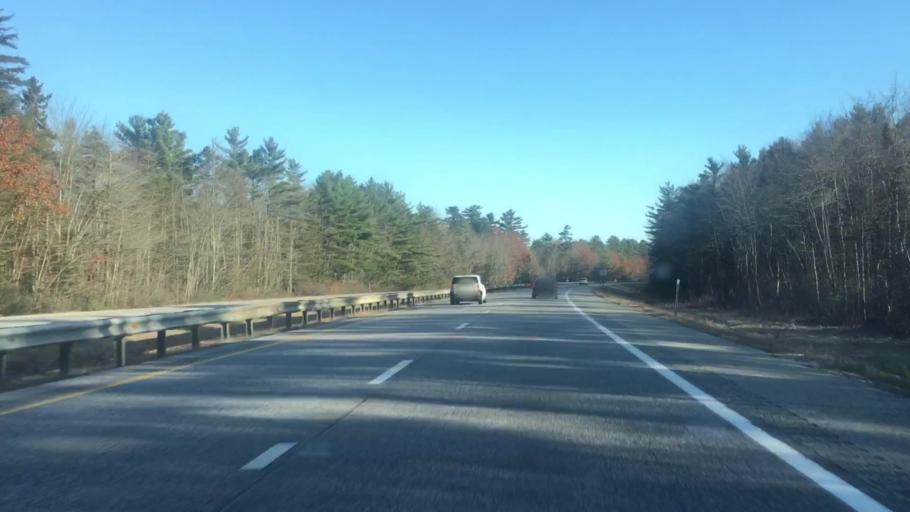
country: US
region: Maine
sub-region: Cumberland County
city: New Gloucester
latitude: 43.9704
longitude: -70.3232
